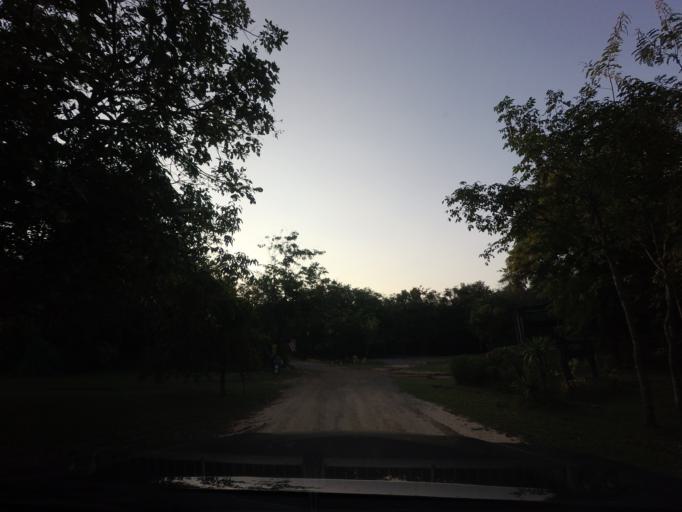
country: TH
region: Nan
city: Na Noi
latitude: 18.3041
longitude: 100.7529
